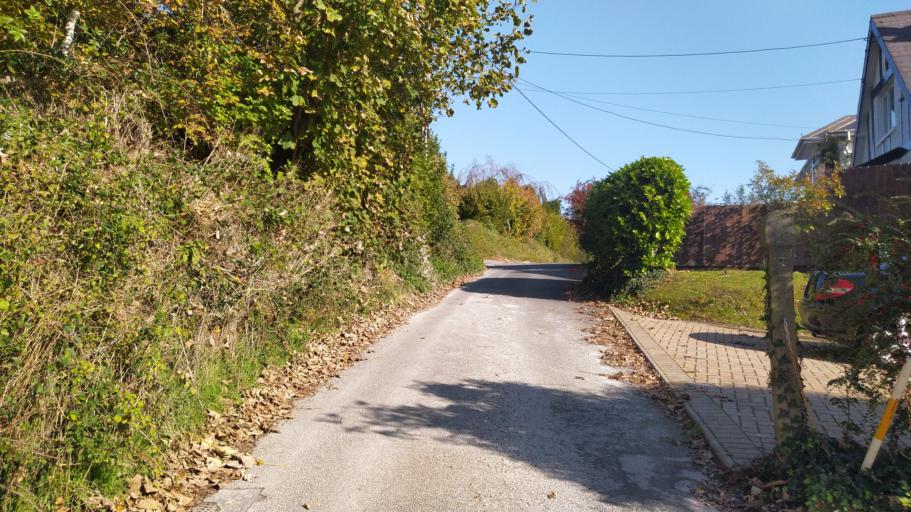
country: GB
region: England
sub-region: Isle of Wight
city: Newport
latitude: 50.6895
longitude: -1.3206
